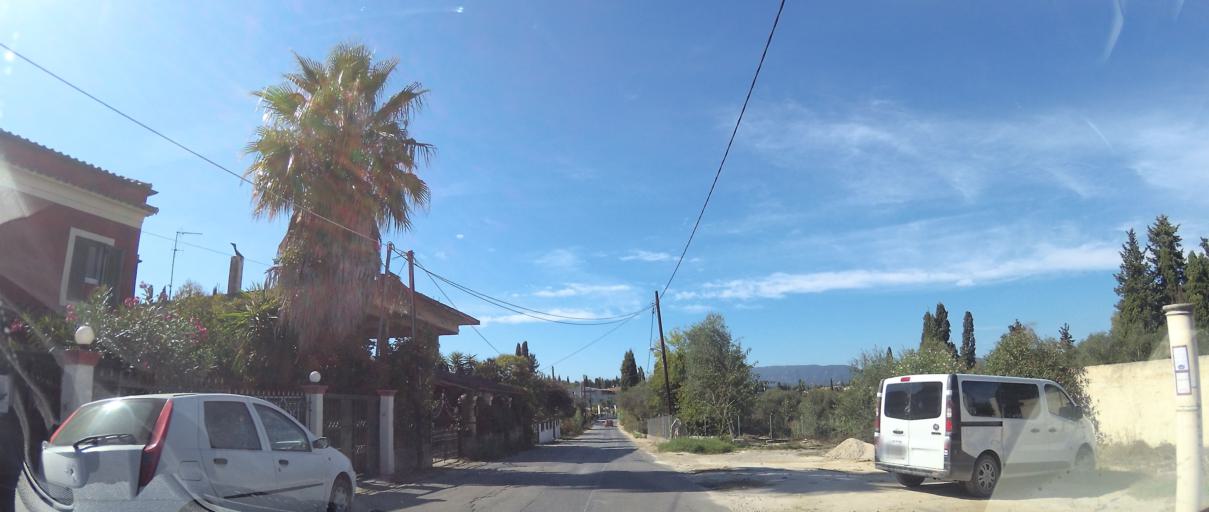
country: GR
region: Ionian Islands
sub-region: Nomos Kerkyras
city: Kontokali
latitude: 39.6441
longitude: 19.8480
